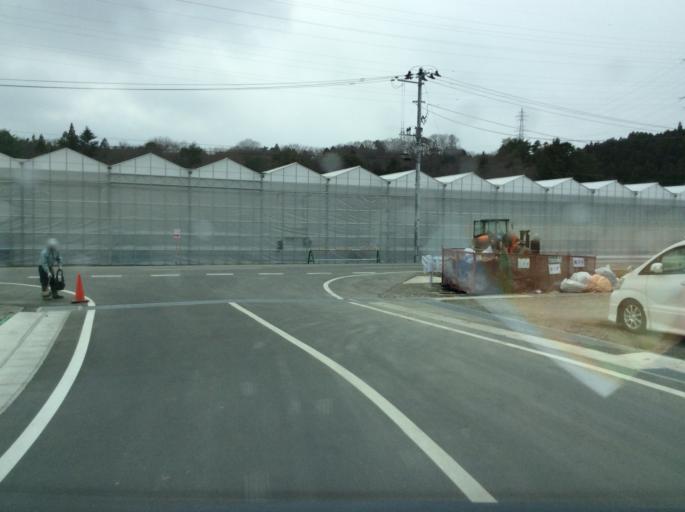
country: JP
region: Fukushima
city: Iwaki
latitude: 37.1221
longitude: 140.9495
